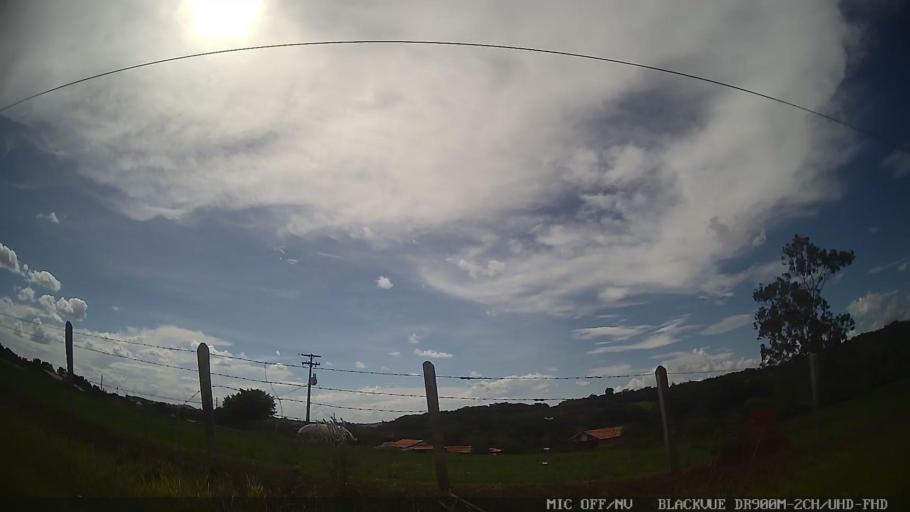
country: BR
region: Sao Paulo
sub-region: Conchas
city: Conchas
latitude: -22.9915
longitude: -47.9975
